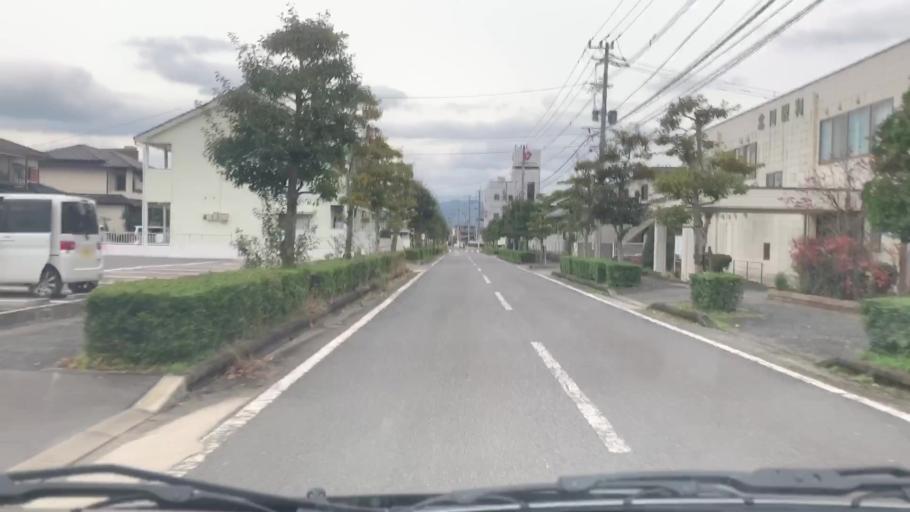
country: JP
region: Saga Prefecture
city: Takeocho-takeo
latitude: 33.1912
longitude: 130.0258
